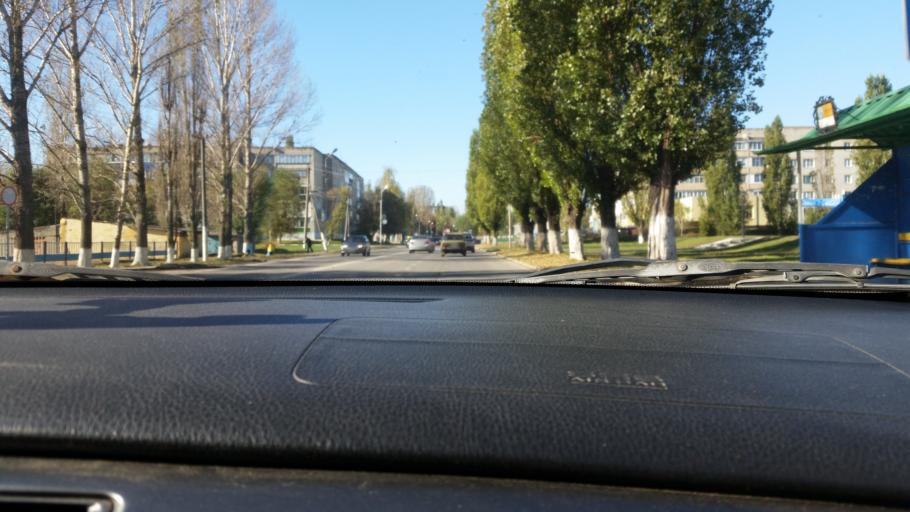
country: RU
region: Lipetsk
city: Gryazi
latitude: 52.4903
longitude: 39.9665
